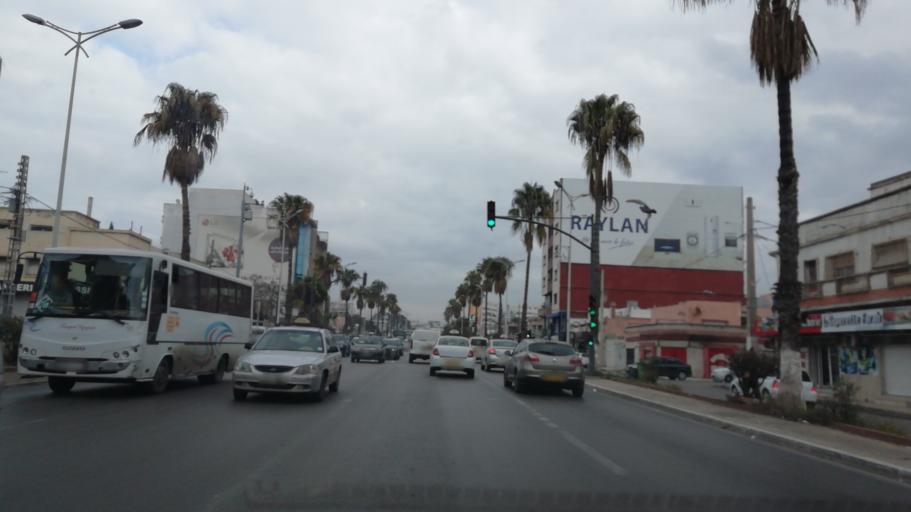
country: DZ
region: Oran
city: Oran
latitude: 35.6944
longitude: -0.6163
